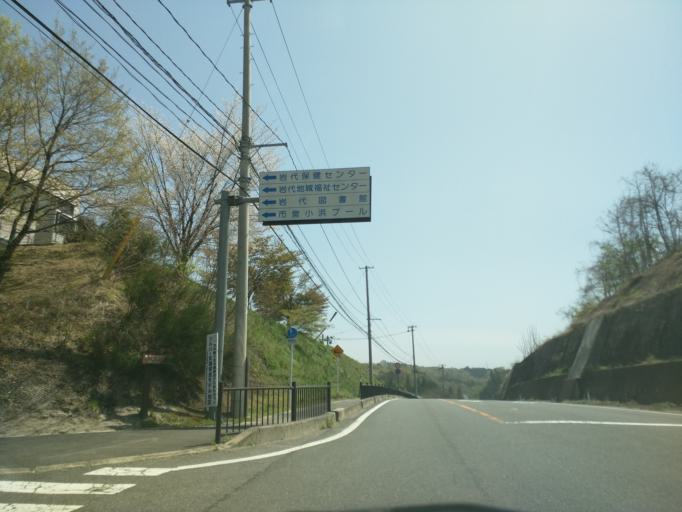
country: JP
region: Fukushima
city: Nihommatsu
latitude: 37.5580
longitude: 140.5142
